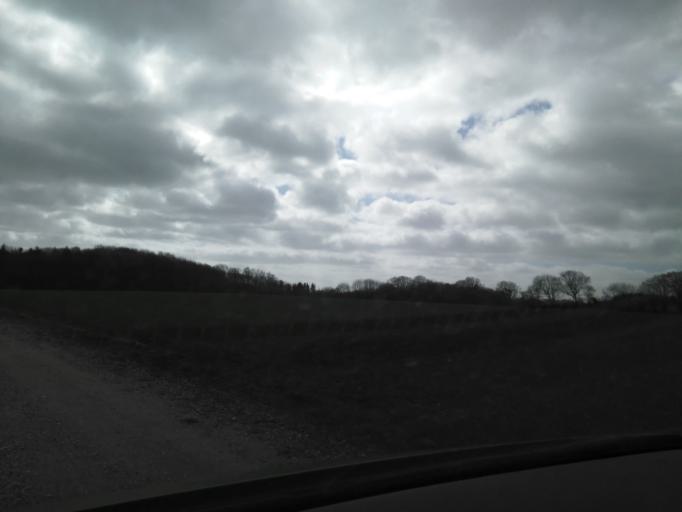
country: DK
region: Central Jutland
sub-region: Arhus Kommune
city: Beder
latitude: 56.0558
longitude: 10.2586
